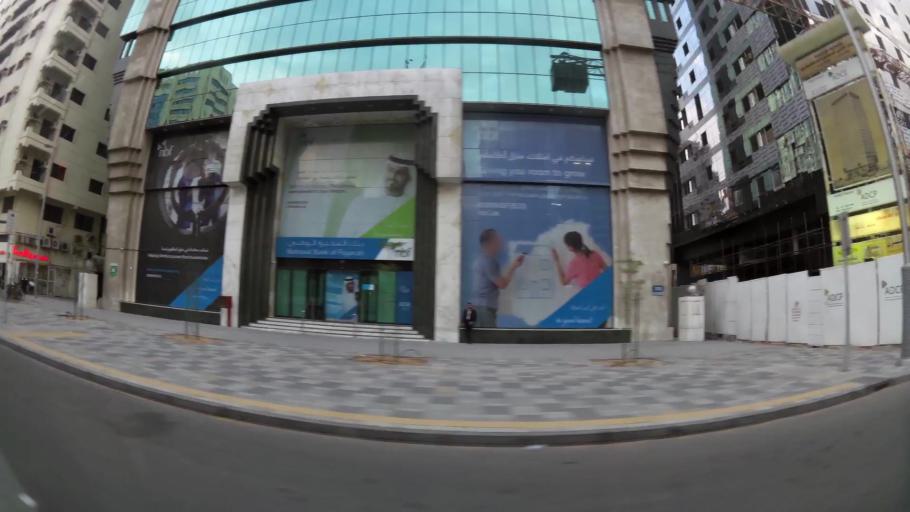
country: AE
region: Abu Dhabi
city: Abu Dhabi
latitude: 24.4976
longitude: 54.3719
